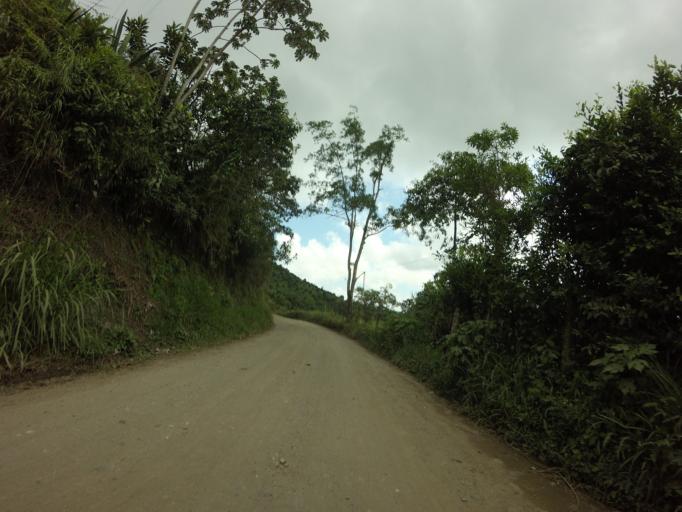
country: CO
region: Caldas
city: Victoria
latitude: 5.3073
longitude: -74.9746
